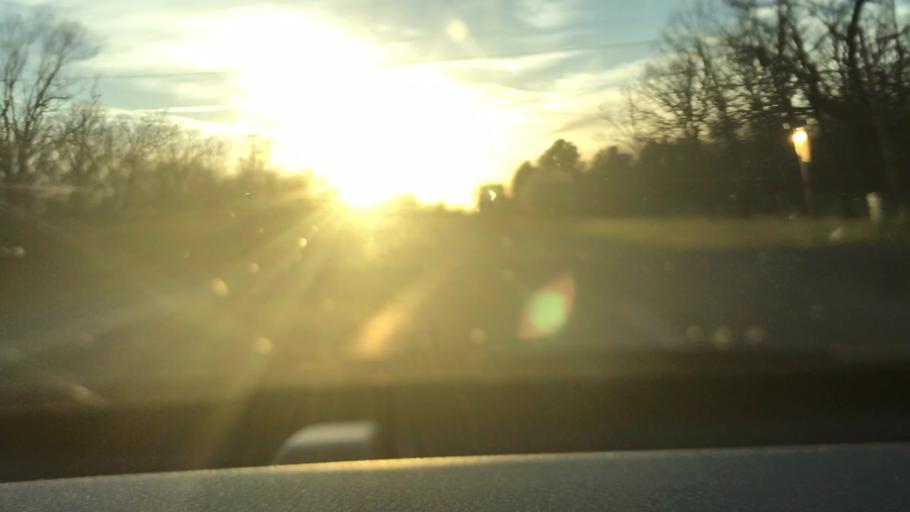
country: US
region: Texas
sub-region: Lamar County
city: Blossom
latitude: 33.6655
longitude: -95.3292
